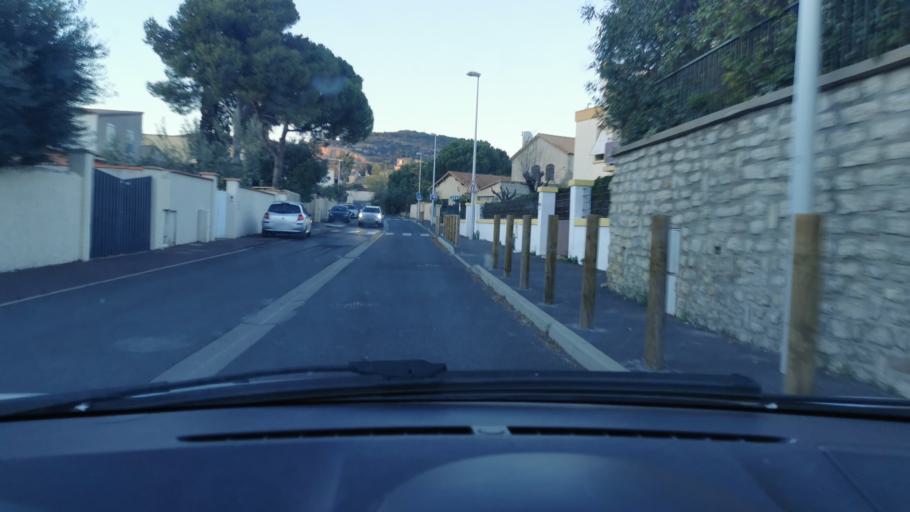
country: FR
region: Languedoc-Roussillon
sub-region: Departement de l'Herault
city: Frontignan
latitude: 43.4538
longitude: 3.7540
